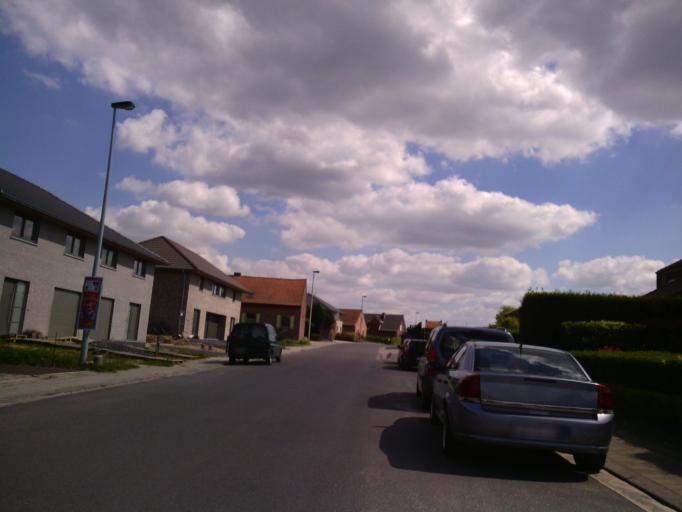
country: BE
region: Flanders
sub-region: Provincie West-Vlaanderen
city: Wevelgem
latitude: 50.7930
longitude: 3.1702
